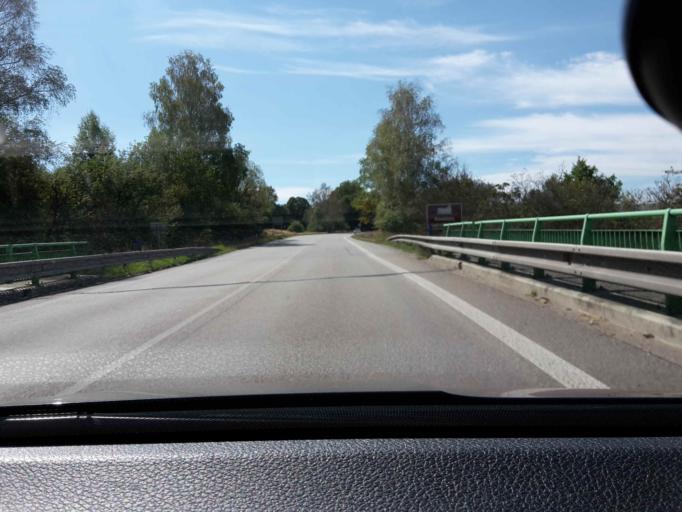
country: CZ
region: Jihocesky
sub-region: Okres Jindrichuv Hradec
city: Jindrichuv Hradec
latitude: 49.1618
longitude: 15.0277
